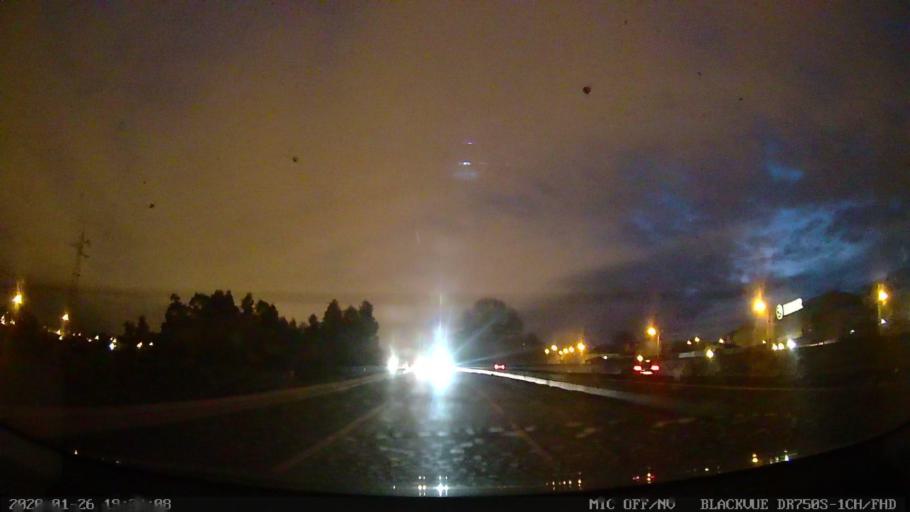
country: PT
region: Porto
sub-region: Maia
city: Leca do Bailio
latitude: 41.1949
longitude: -8.6277
